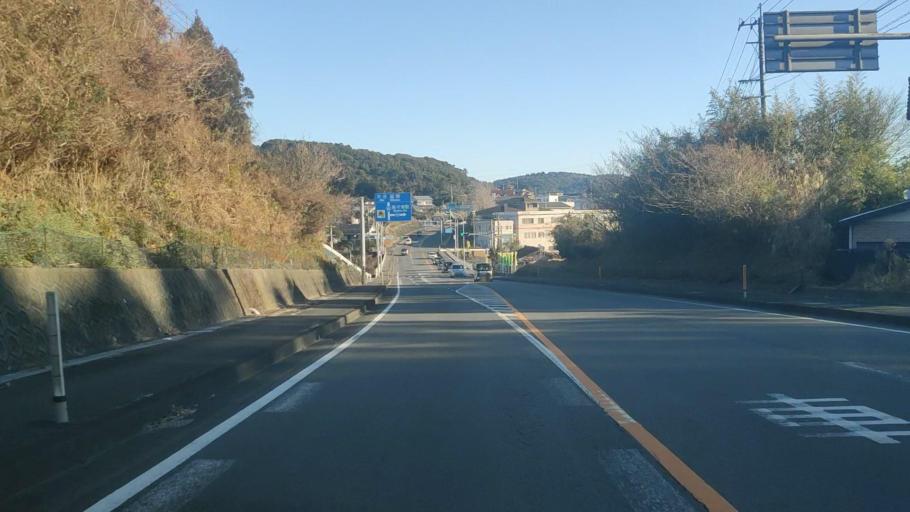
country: JP
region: Miyazaki
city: Takanabe
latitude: 32.3291
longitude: 131.6029
